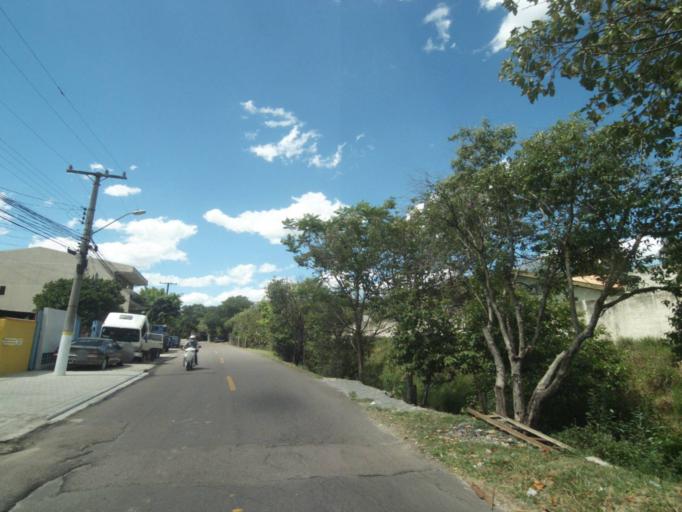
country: BR
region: Parana
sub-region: Curitiba
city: Curitiba
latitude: -25.5093
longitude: -49.3286
